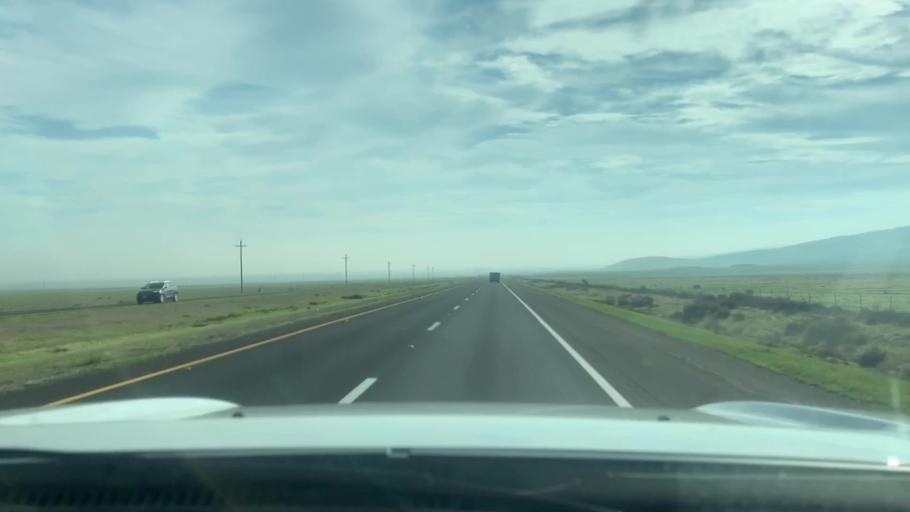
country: US
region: California
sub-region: San Luis Obispo County
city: Shandon
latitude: 35.6571
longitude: -120.0531
